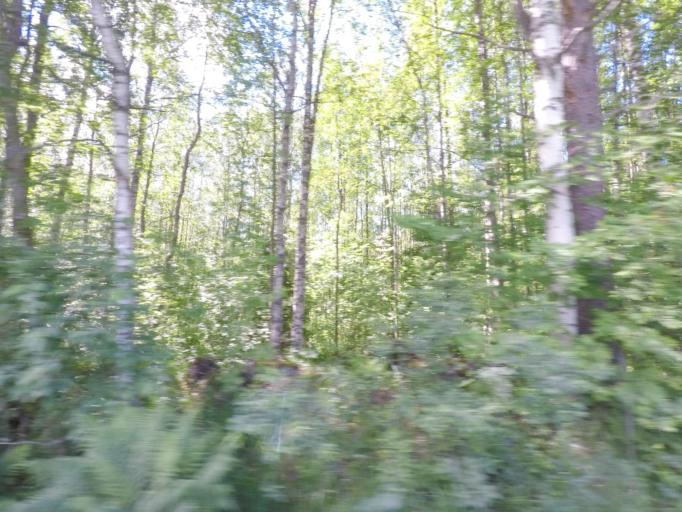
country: FI
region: Central Finland
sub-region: Jyvaeskylae
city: Hankasalmi
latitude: 62.4372
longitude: 26.6461
